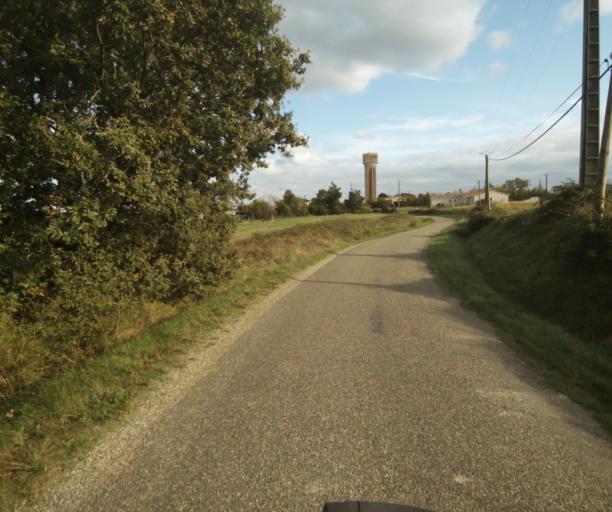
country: FR
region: Midi-Pyrenees
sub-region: Departement de la Haute-Garonne
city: Launac
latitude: 43.8244
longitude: 1.1150
